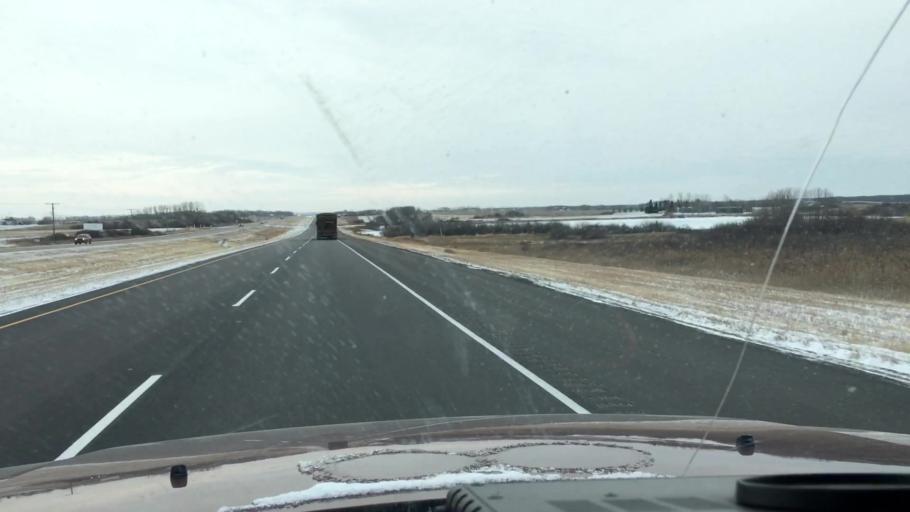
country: CA
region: Saskatchewan
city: Saskatoon
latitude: 51.9252
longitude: -106.5331
